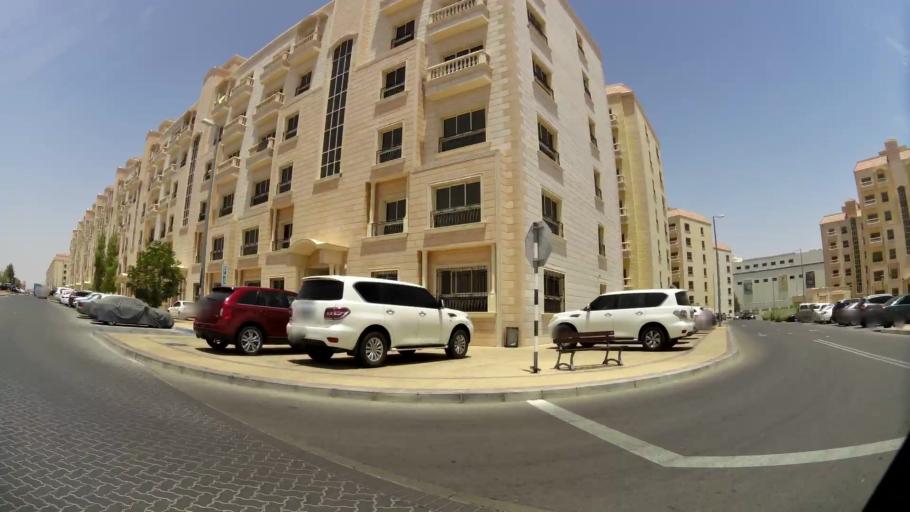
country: OM
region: Al Buraimi
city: Al Buraymi
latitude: 24.2709
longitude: 55.7795
